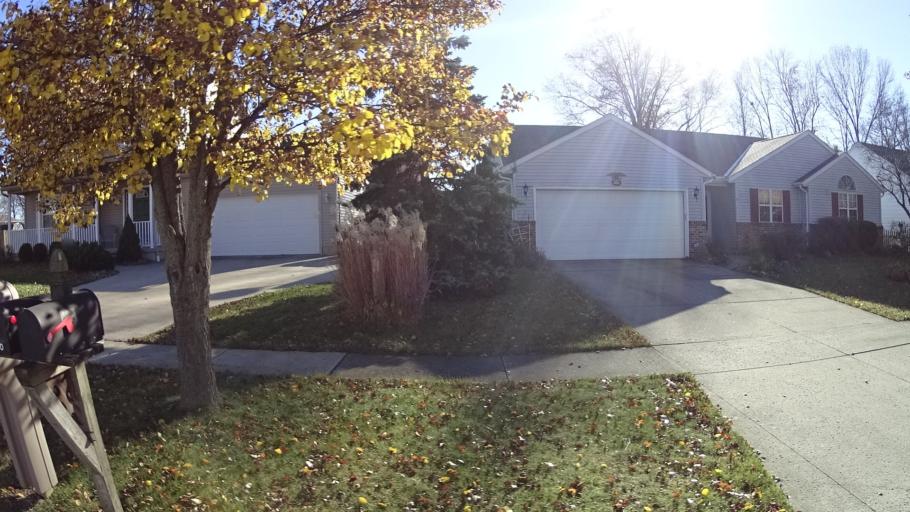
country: US
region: Ohio
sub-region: Lorain County
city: Elyria
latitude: 41.3486
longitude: -82.0825
